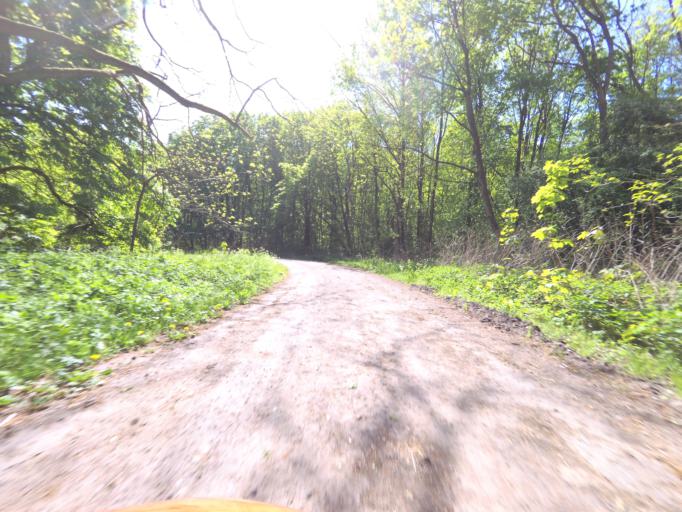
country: NL
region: Gelderland
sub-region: Gemeente Harderwijk
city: Harderwijk
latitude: 52.4010
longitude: 5.6252
